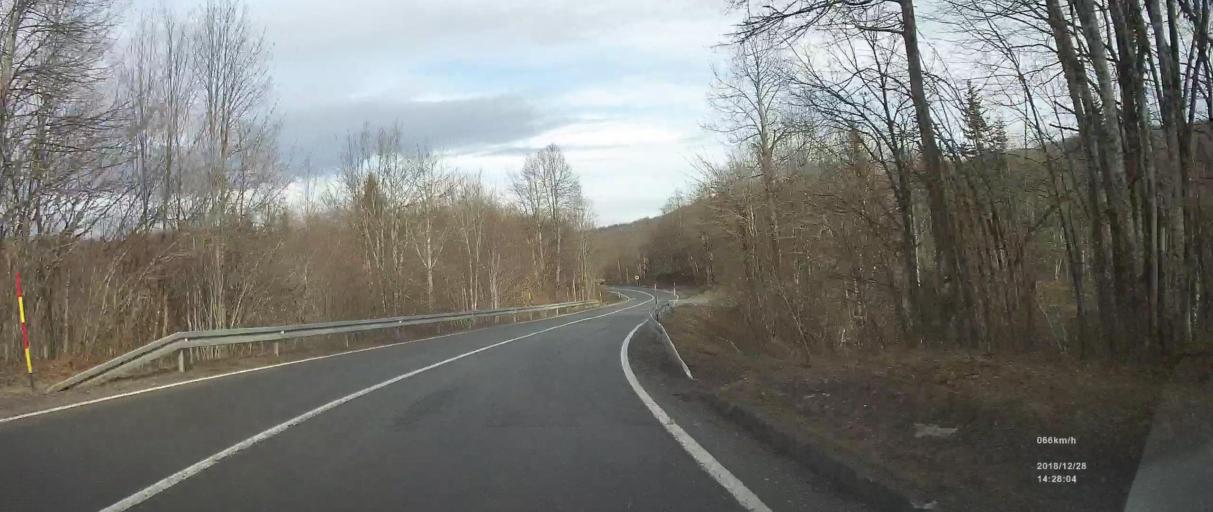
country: HR
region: Primorsko-Goranska
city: Vrbovsko
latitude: 45.4072
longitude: 15.1102
